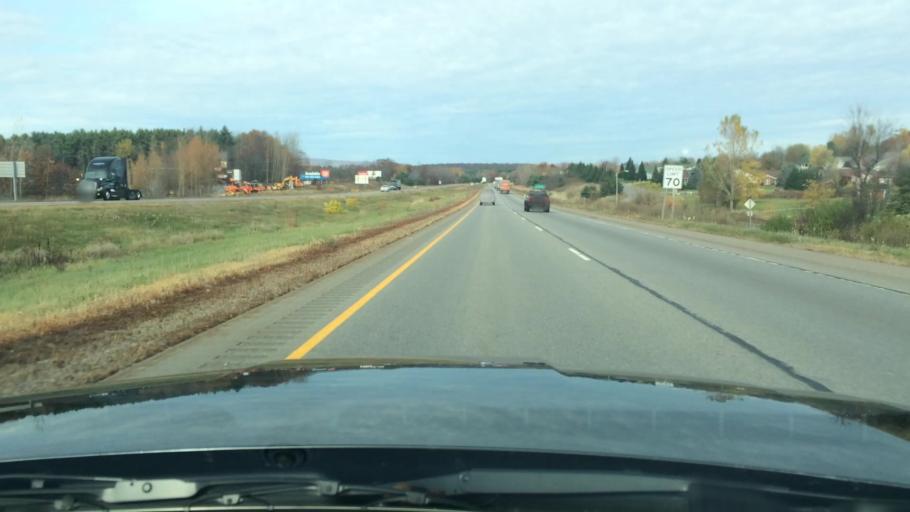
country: US
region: Wisconsin
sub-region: Marathon County
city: Mosinee
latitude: 44.7951
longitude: -89.6794
